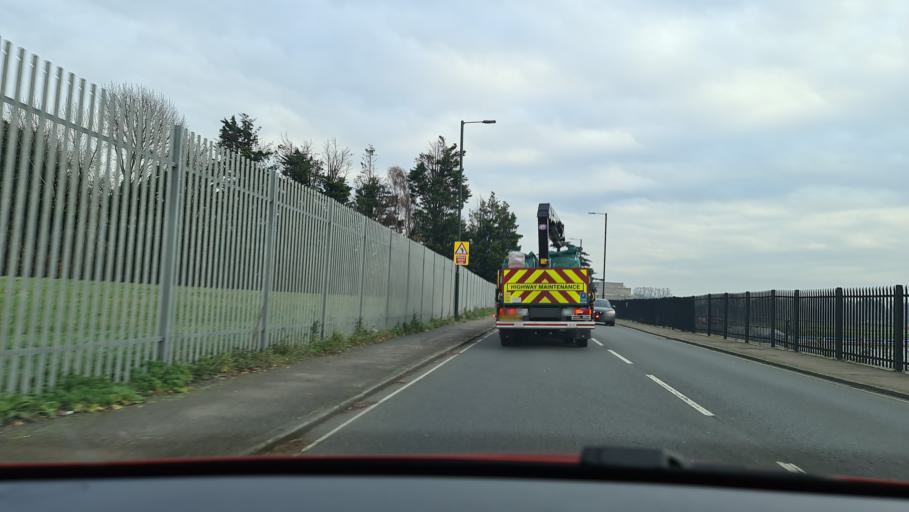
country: GB
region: England
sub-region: Greater London
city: Hampton
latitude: 51.4137
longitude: -0.3807
